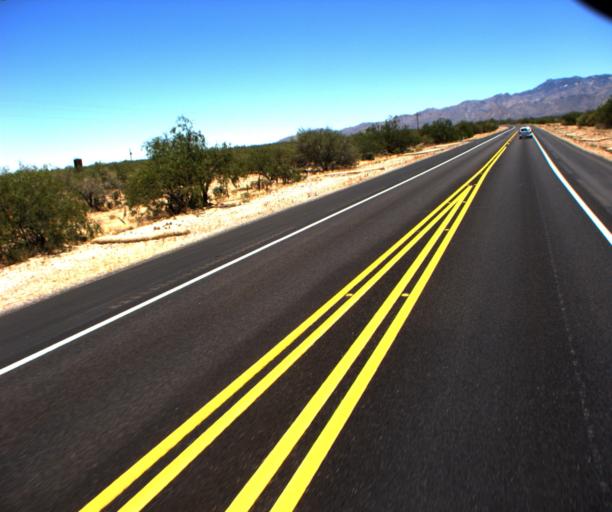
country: US
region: Arizona
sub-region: Pima County
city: Sells
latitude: 31.9284
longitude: -111.7903
